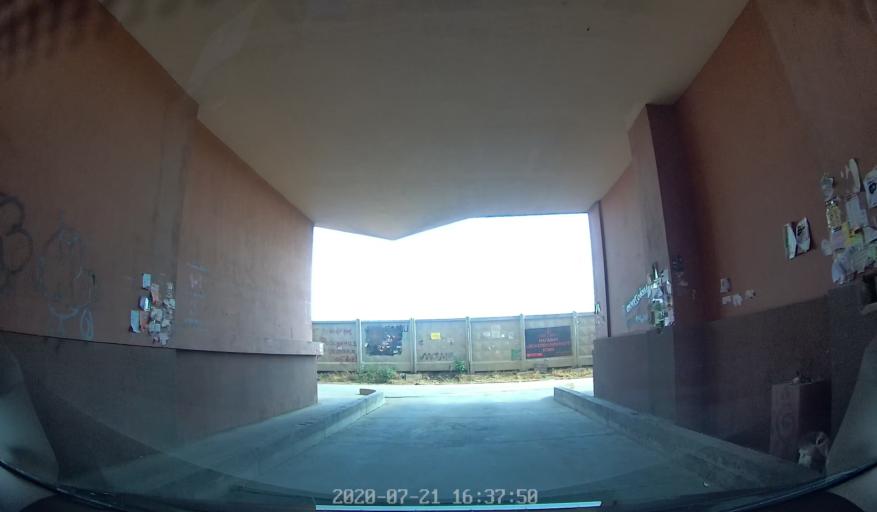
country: GR
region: South Aegean
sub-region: Nomos Kykladon
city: Serifos
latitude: 37.1205
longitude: 24.5641
